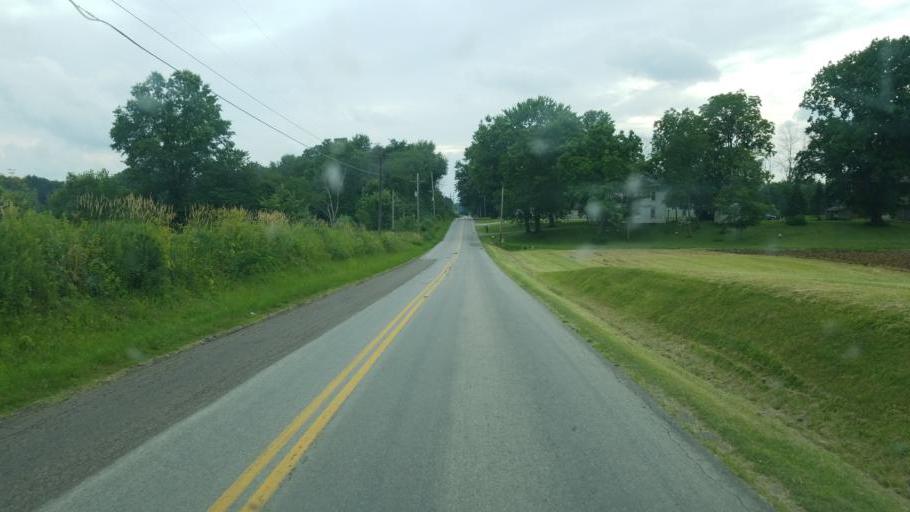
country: US
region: Ohio
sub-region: Wayne County
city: Orrville
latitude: 40.8221
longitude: -81.7701
